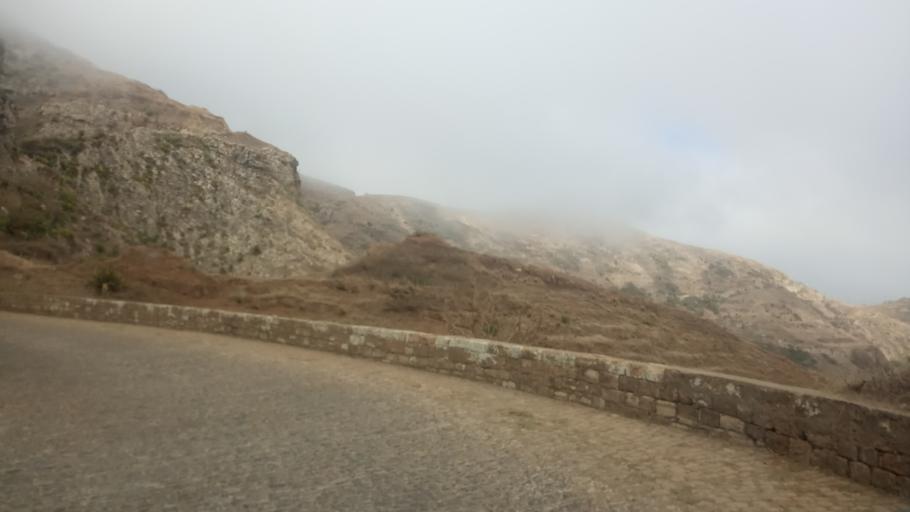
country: CV
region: Brava
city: Vila Nova Sintra
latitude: 14.8681
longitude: -24.7066
